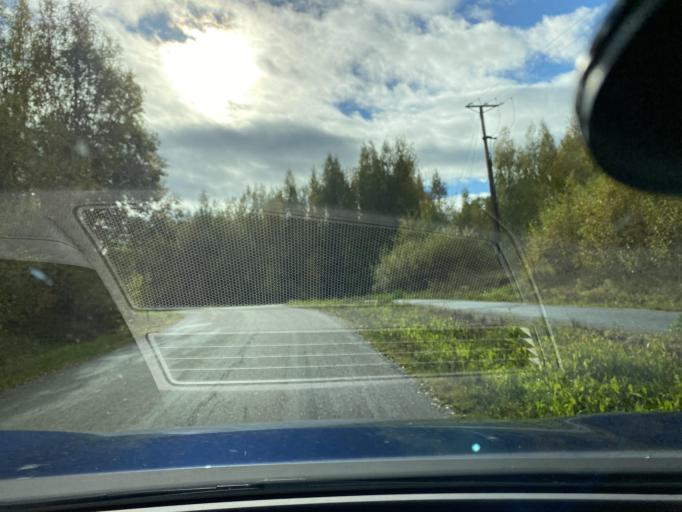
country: FI
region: Pirkanmaa
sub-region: Tampere
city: Nokia
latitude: 61.4733
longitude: 23.3533
